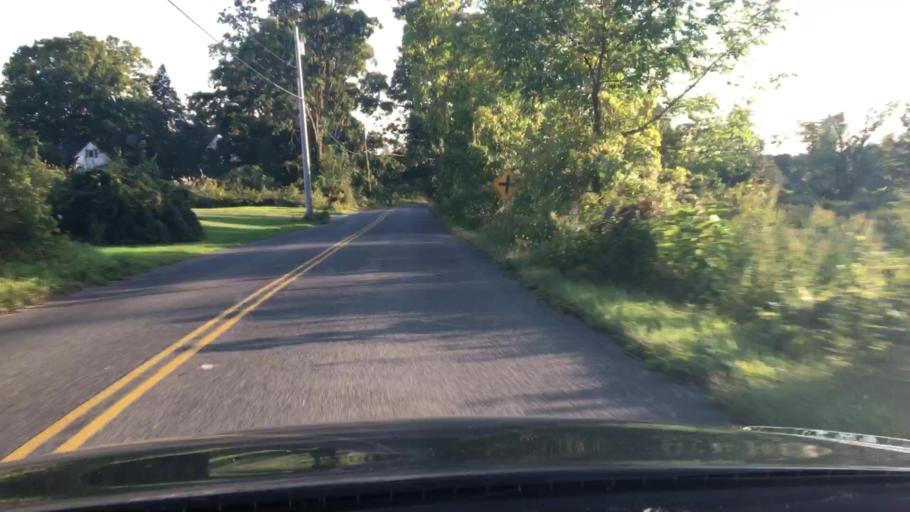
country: US
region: Connecticut
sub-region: Litchfield County
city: New Milford
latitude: 41.6098
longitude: -73.3721
